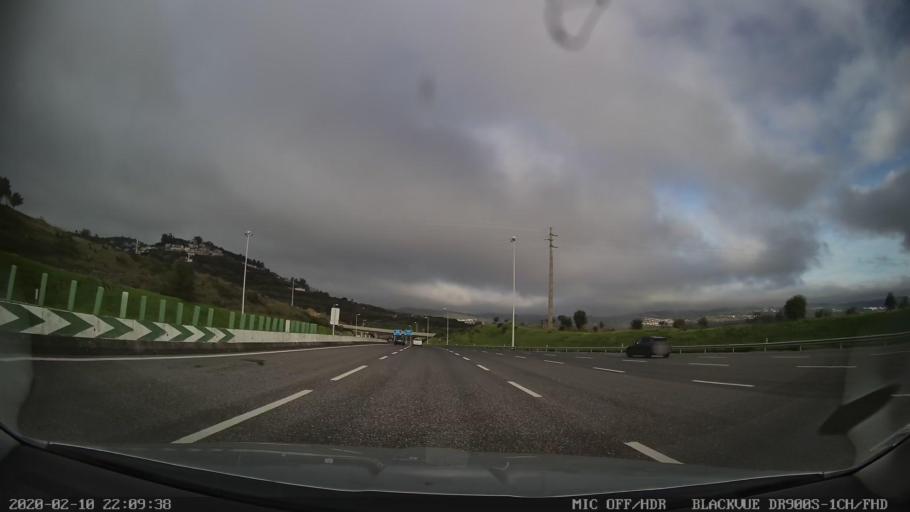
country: PT
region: Lisbon
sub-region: Odivelas
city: Ramada
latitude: 38.8209
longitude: -9.1880
